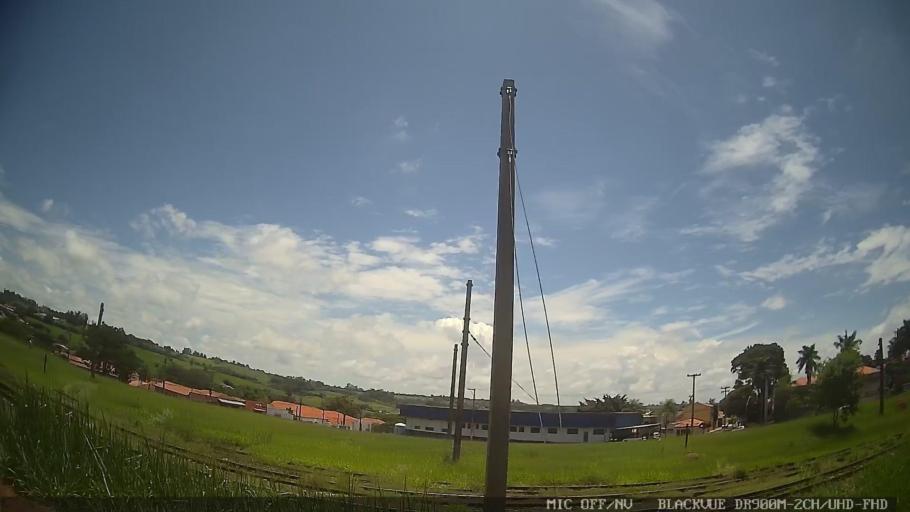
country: BR
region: Sao Paulo
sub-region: Laranjal Paulista
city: Laranjal Paulista
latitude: -23.0445
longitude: -47.8377
